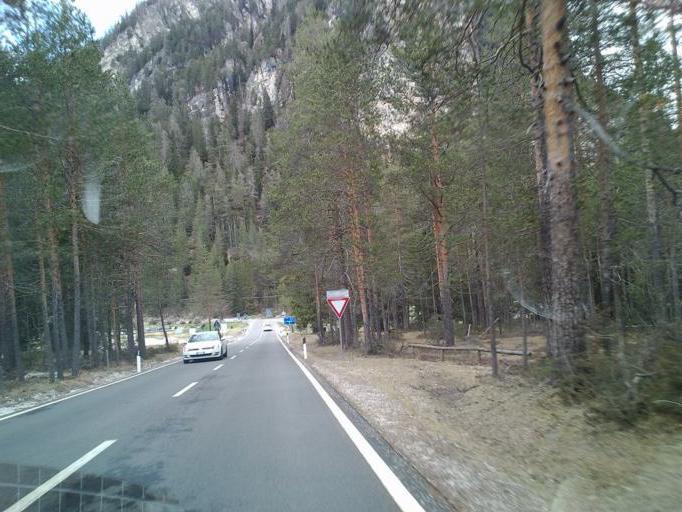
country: IT
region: Trentino-Alto Adige
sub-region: Bolzano
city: Dobbiaco
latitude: 46.6198
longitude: 12.2198
